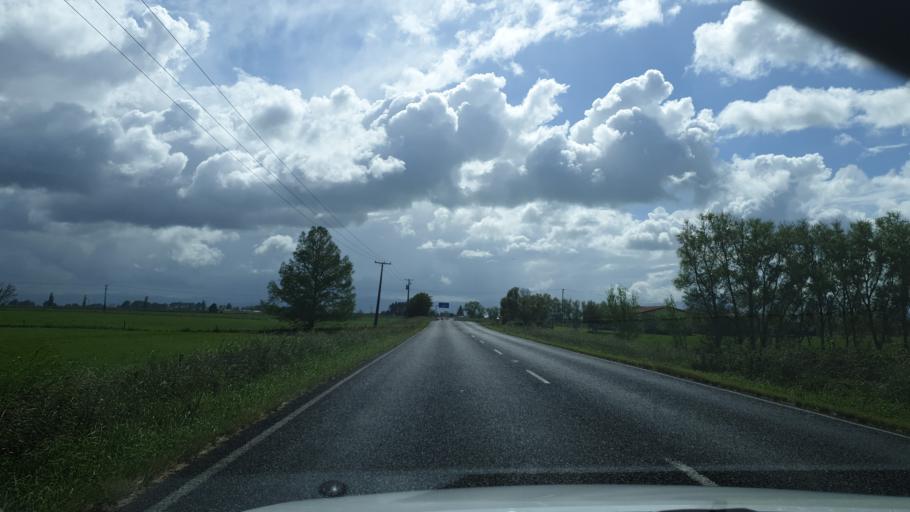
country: NZ
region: Waikato
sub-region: Hauraki District
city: Paeroa
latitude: -37.5120
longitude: 175.5183
